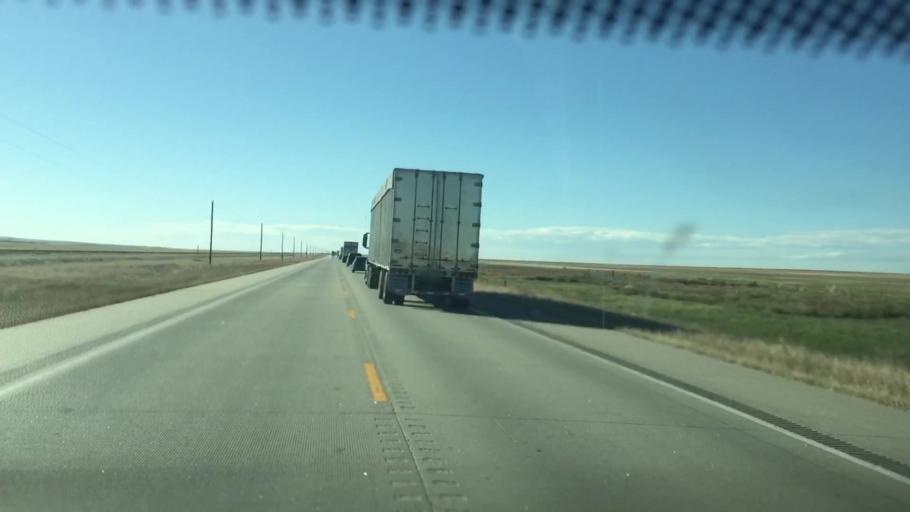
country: US
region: Colorado
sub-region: Kiowa County
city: Eads
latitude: 38.8324
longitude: -103.0519
